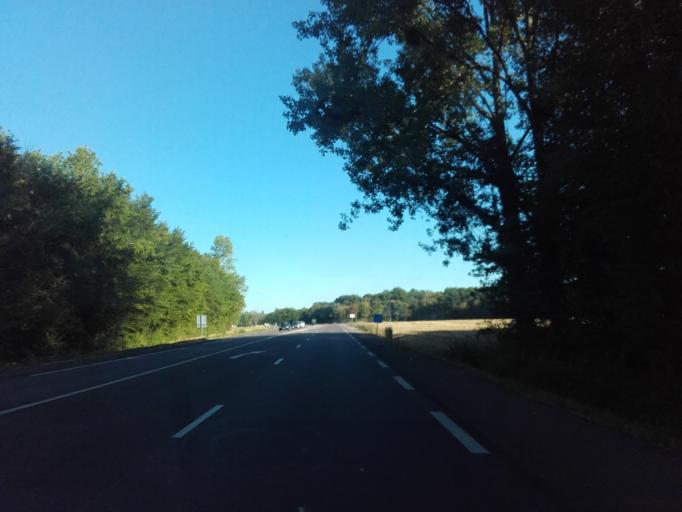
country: FR
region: Bourgogne
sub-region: Departement de Saone-et-Loire
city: Fontaines
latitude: 46.8706
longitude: 4.7902
